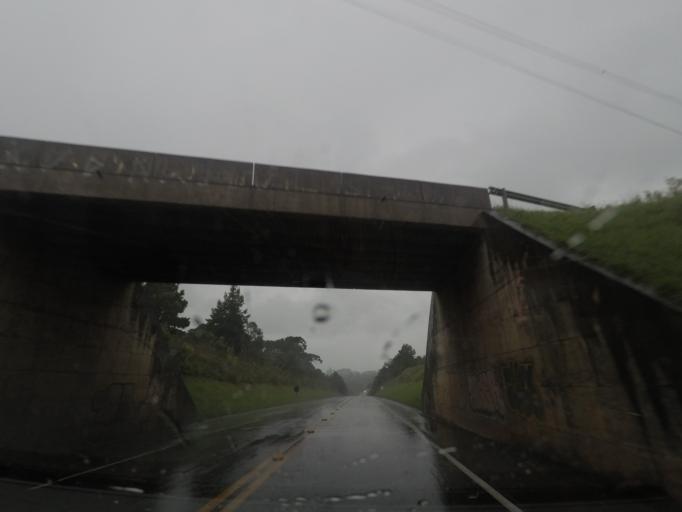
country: BR
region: Parana
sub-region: Almirante Tamandare
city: Almirante Tamandare
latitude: -25.3591
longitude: -49.3123
